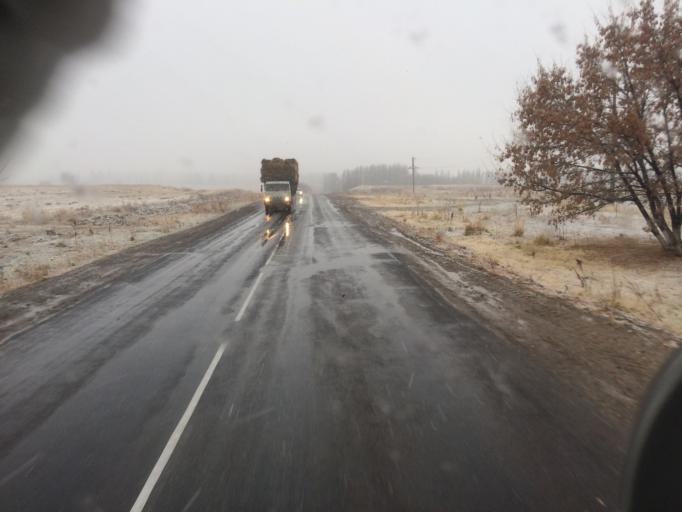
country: KG
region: Chuy
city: Ivanovka
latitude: 42.9649
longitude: 75.0057
